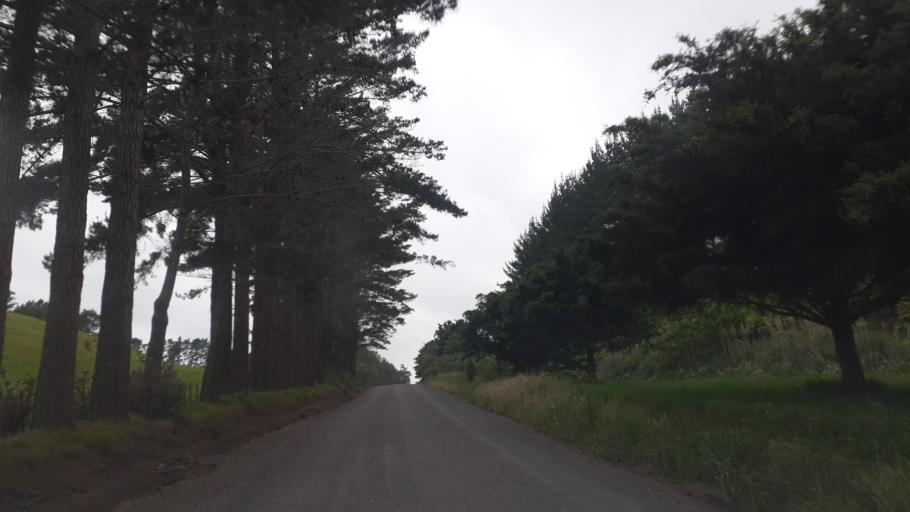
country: NZ
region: Northland
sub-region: Far North District
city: Kerikeri
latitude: -35.2799
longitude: 173.9626
